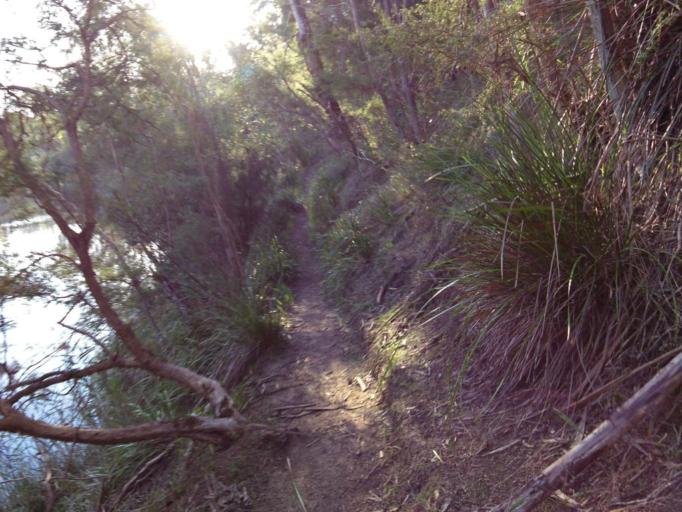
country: AU
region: Victoria
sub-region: Manningham
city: Warrandyte
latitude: -37.7328
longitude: 145.2426
